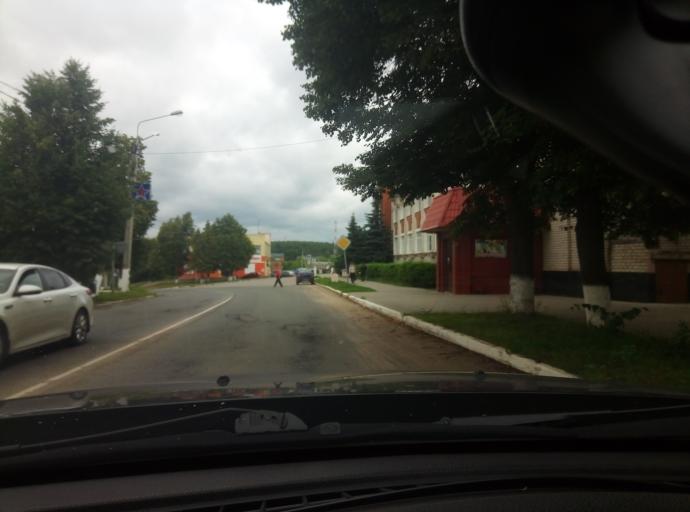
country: RU
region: Kaluga
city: Zhukovo
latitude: 55.0310
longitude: 36.7467
